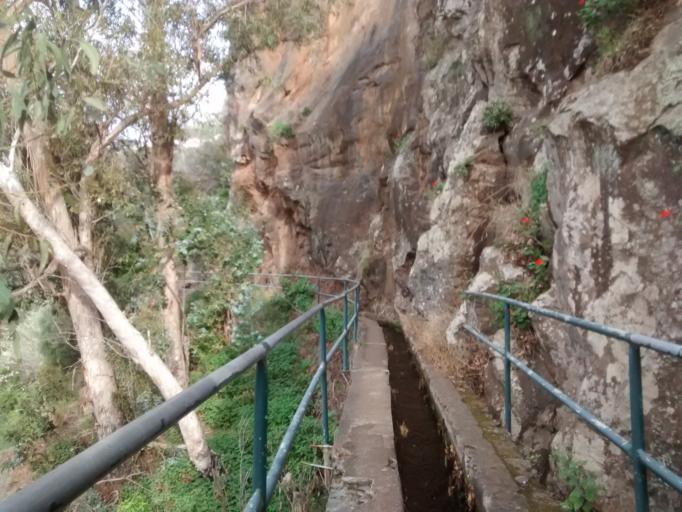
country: PT
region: Madeira
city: Camara de Lobos
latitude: 32.6602
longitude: -16.9600
